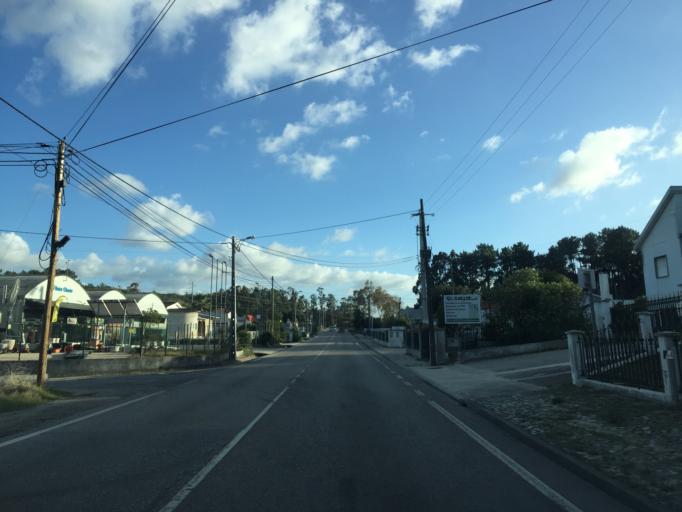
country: PT
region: Leiria
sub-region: Leiria
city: Souto da Carpalhosa
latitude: 39.8258
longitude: -8.8400
